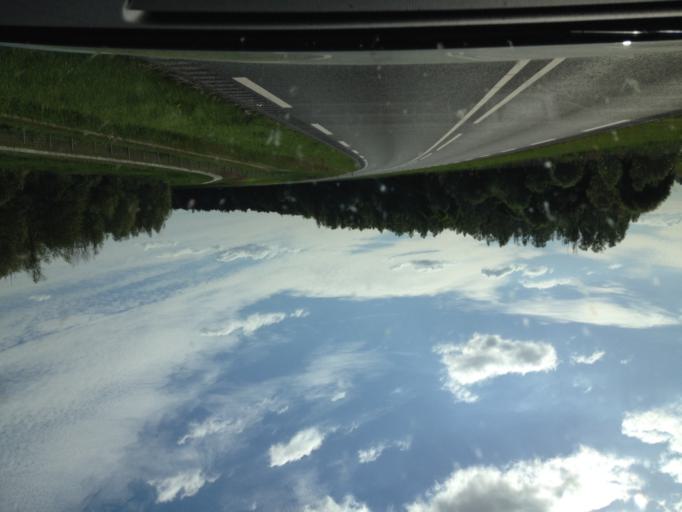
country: NL
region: Gelderland
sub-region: Gemeente Nijkerk
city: Nijkerk
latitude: 52.2628
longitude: 5.4632
